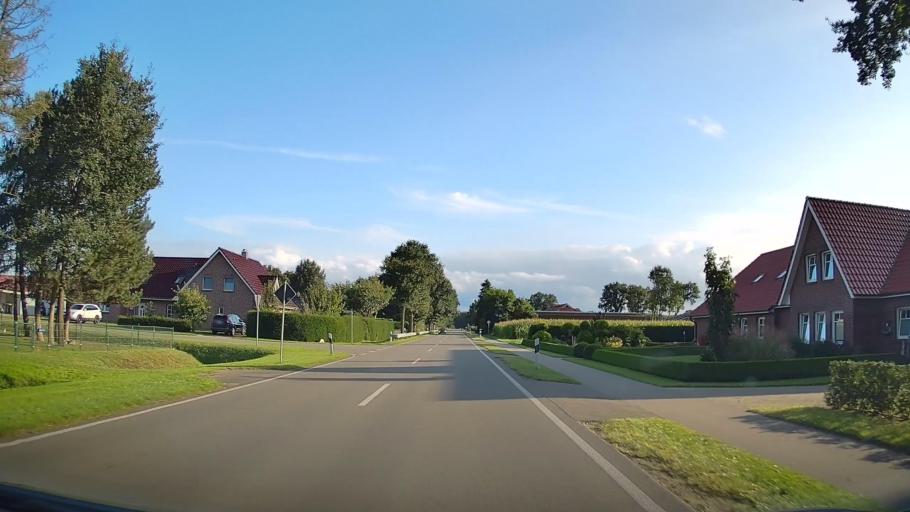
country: DE
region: Lower Saxony
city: Barssel
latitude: 53.0954
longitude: 7.7118
